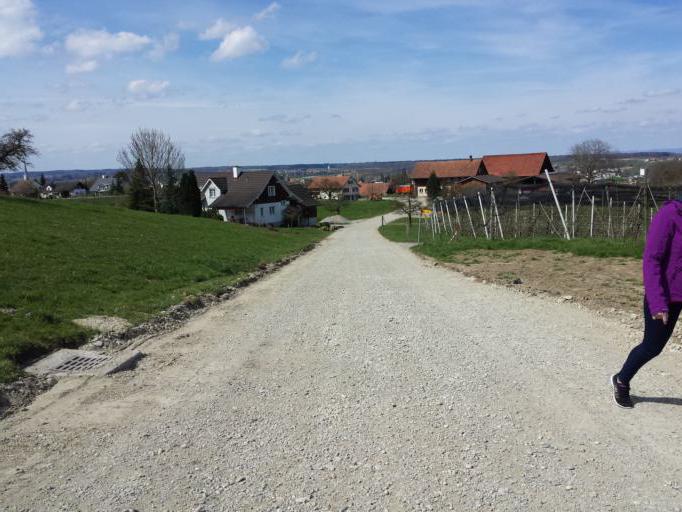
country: CH
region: Thurgau
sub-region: Arbon District
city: Amriswil
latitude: 47.5371
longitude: 9.3119
